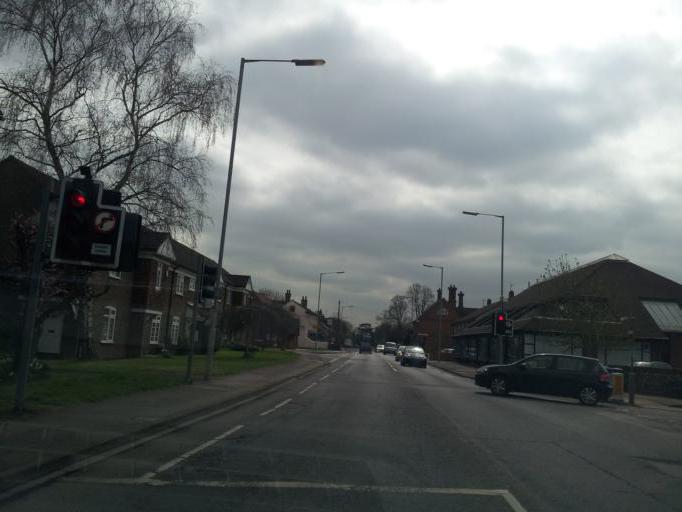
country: GB
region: England
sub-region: Cambridgeshire
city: Grantchester
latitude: 52.1755
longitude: 0.1127
